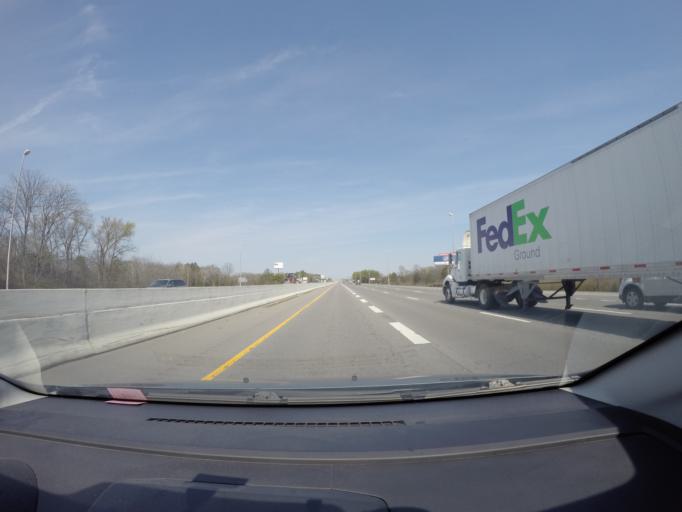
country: US
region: Tennessee
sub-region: Rutherford County
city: Murfreesboro
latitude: 35.8334
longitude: -86.4199
